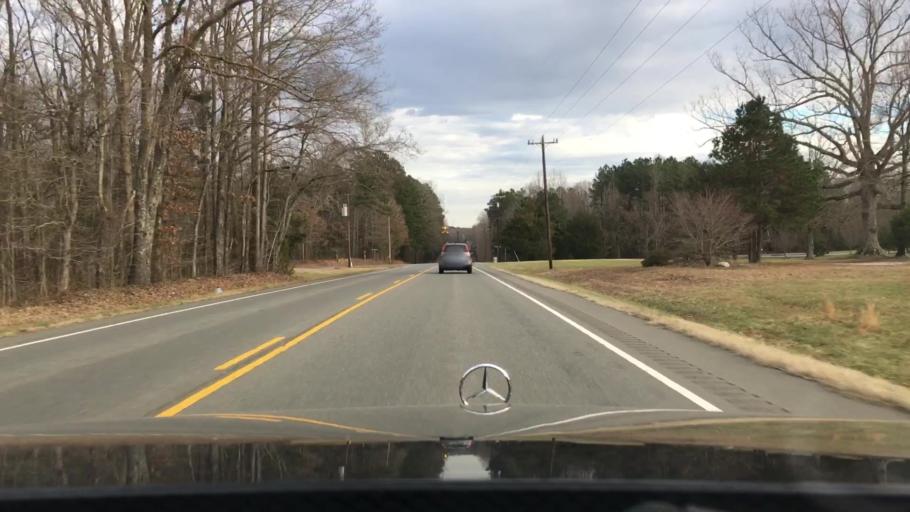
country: US
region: North Carolina
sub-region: Orange County
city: Hillsborough
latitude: 36.2079
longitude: -79.1587
